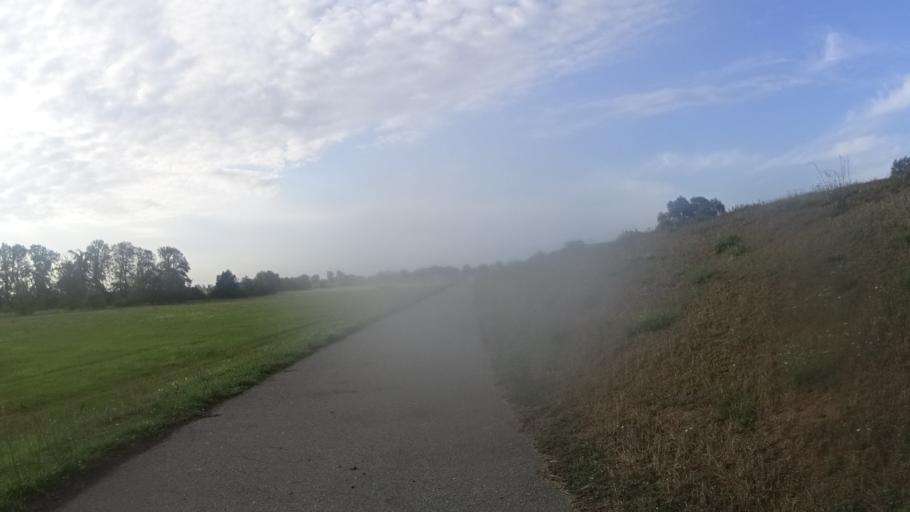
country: DE
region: Brandenburg
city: Lanz
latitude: 53.0474
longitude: 11.5739
